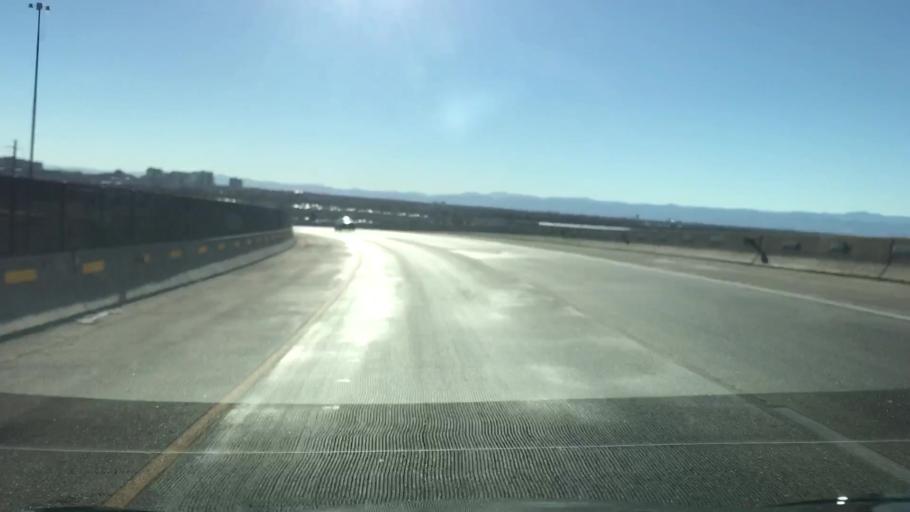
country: US
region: Colorado
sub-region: Adams County
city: Aurora
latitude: 39.7710
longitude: -104.8271
